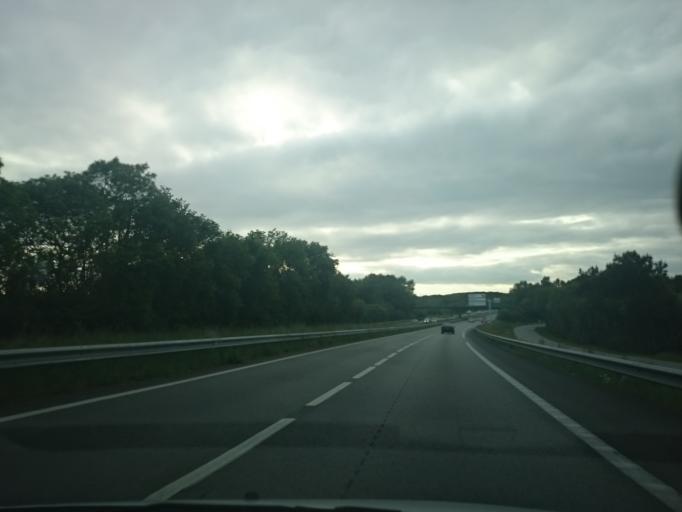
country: FR
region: Brittany
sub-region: Departement du Morbihan
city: Landaul
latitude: 47.7266
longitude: -3.0840
